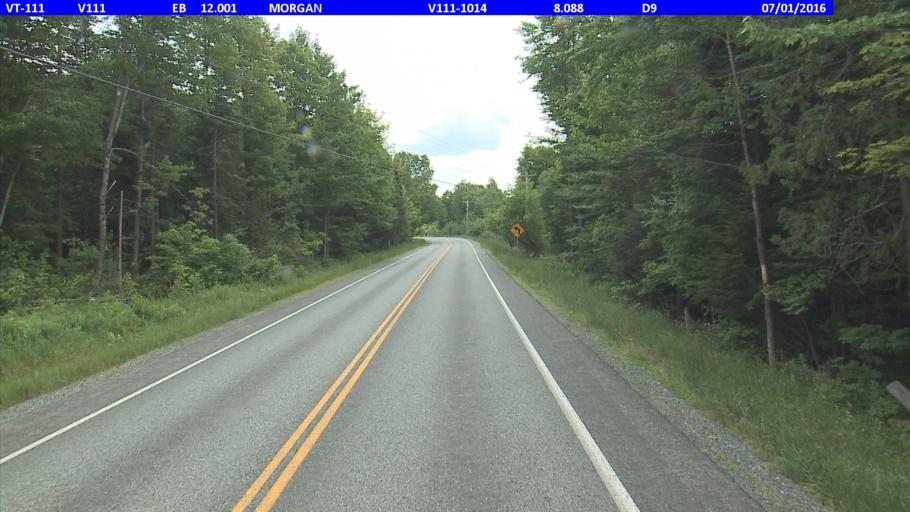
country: US
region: Vermont
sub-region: Orleans County
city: Newport
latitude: 44.8676
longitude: -71.9577
